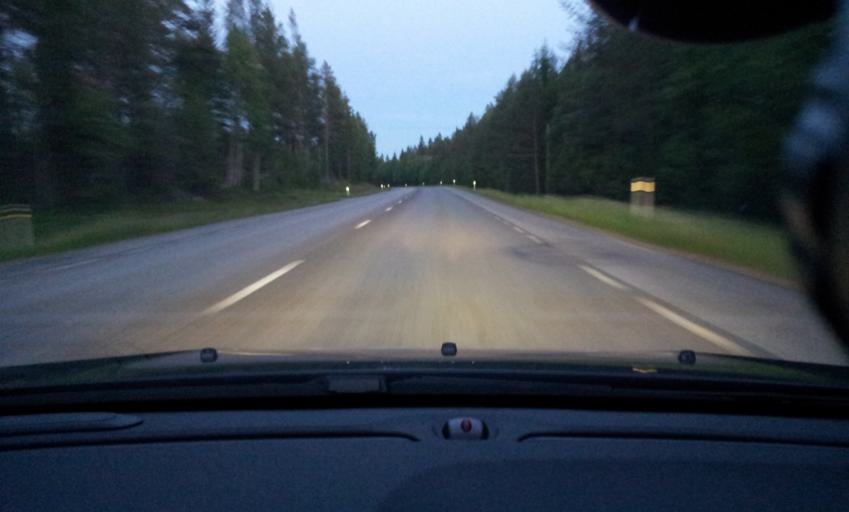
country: SE
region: Jaemtland
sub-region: Braecke Kommun
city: Braecke
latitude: 62.7332
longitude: 15.4348
